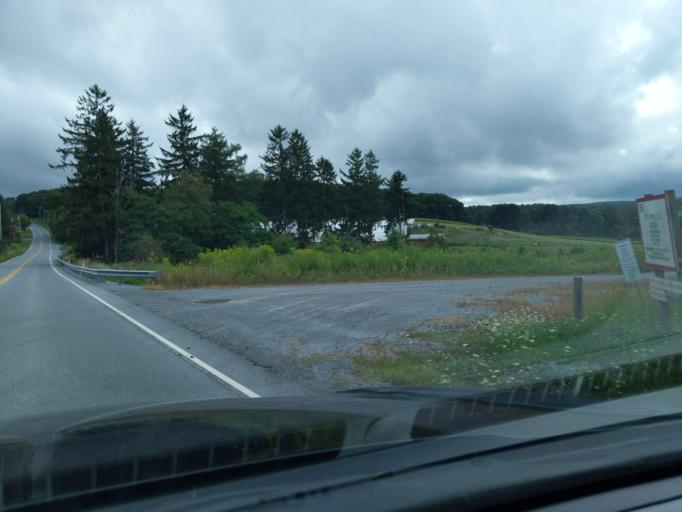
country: US
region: Pennsylvania
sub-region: Cambria County
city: Cresson
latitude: 40.3542
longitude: -78.5652
